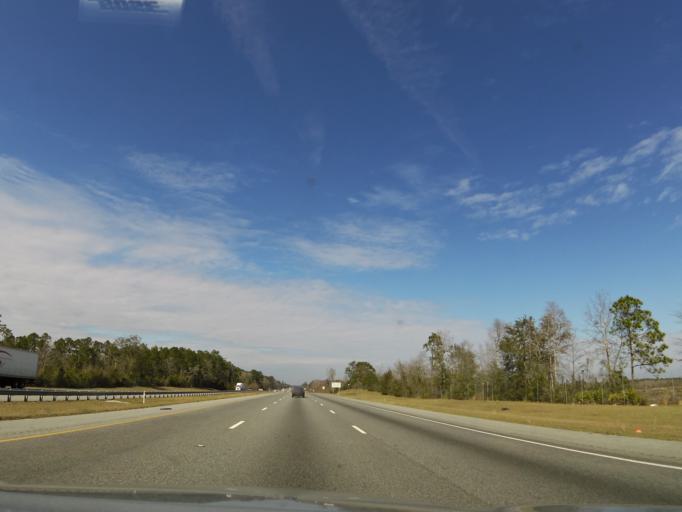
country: US
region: Georgia
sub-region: McIntosh County
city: Darien
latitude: 31.4329
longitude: -81.4437
